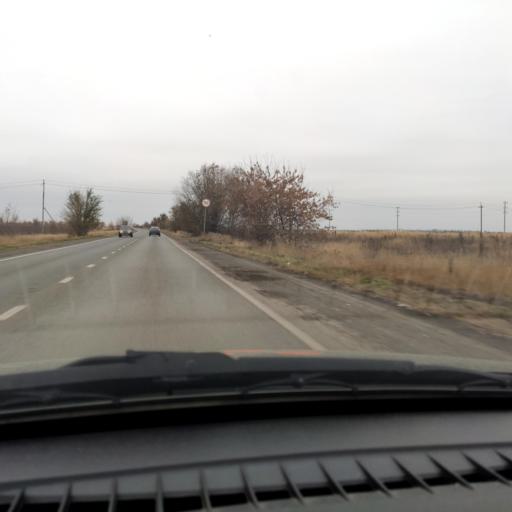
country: RU
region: Samara
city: Podstepki
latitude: 53.5172
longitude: 49.2126
